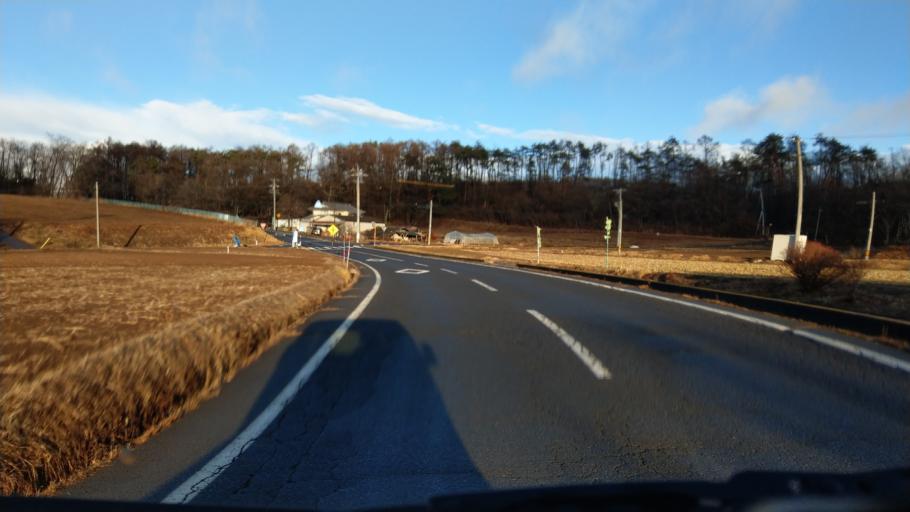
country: JP
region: Nagano
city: Komoro
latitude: 36.3061
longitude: 138.3847
